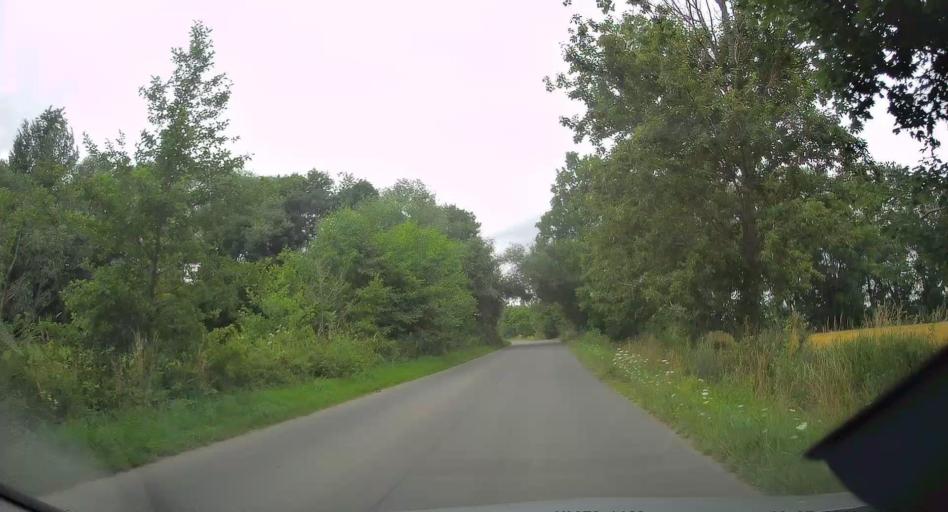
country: PL
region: Lower Silesian Voivodeship
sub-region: Powiat zabkowicki
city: Budzow
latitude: 50.5586
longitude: 16.6961
